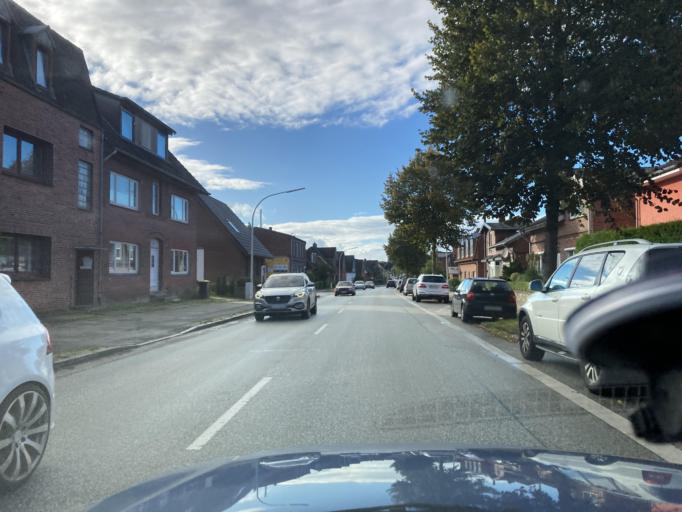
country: DE
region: Schleswig-Holstein
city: Rendsburg
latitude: 54.3086
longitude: 9.6409
